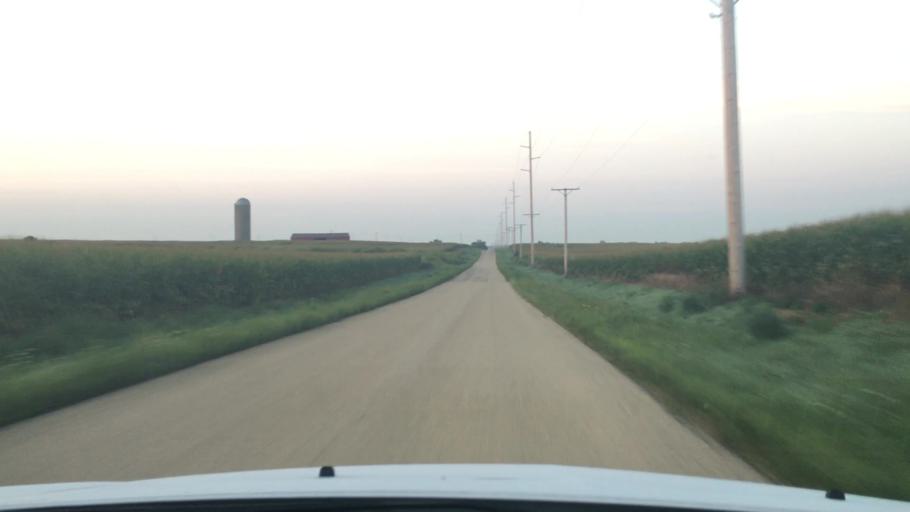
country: US
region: Illinois
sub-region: Ogle County
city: Rochelle
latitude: 41.8606
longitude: -89.0007
